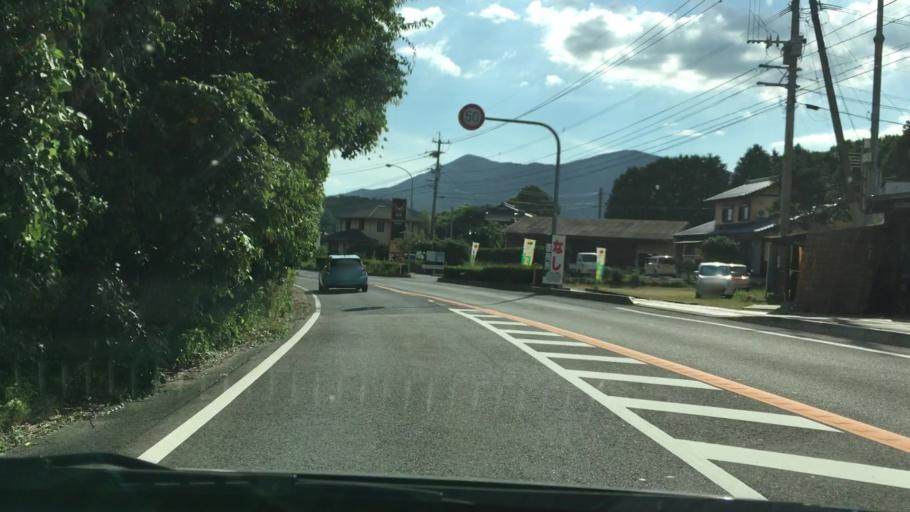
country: JP
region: Saga Prefecture
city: Imaricho-ko
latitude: 33.1868
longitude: 129.8560
